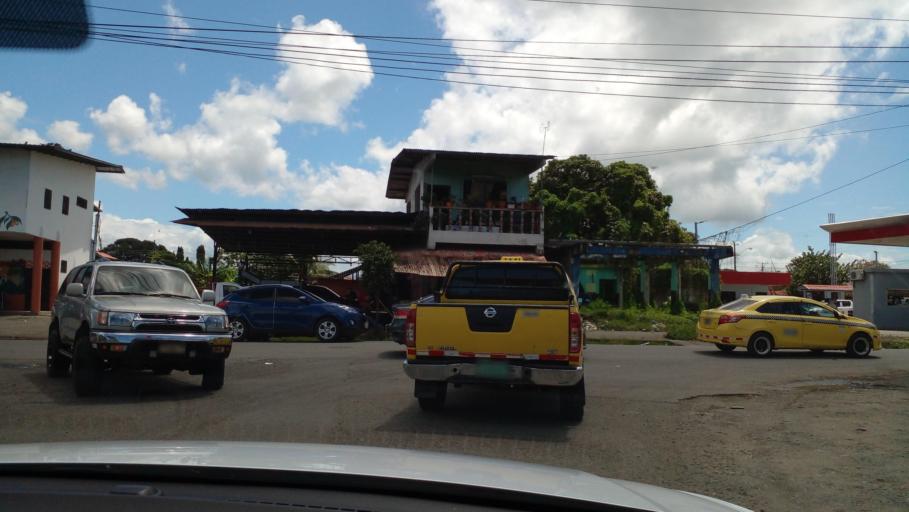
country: PA
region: Bocas del Toro
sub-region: Distrito de Changuinola
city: Changuinola
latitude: 9.4151
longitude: -82.5226
